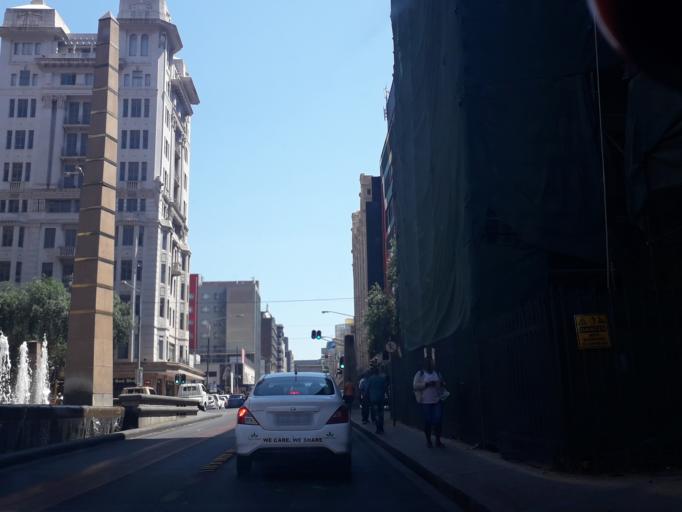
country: ZA
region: Gauteng
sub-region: City of Johannesburg Metropolitan Municipality
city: Johannesburg
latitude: -26.2045
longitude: 28.0421
